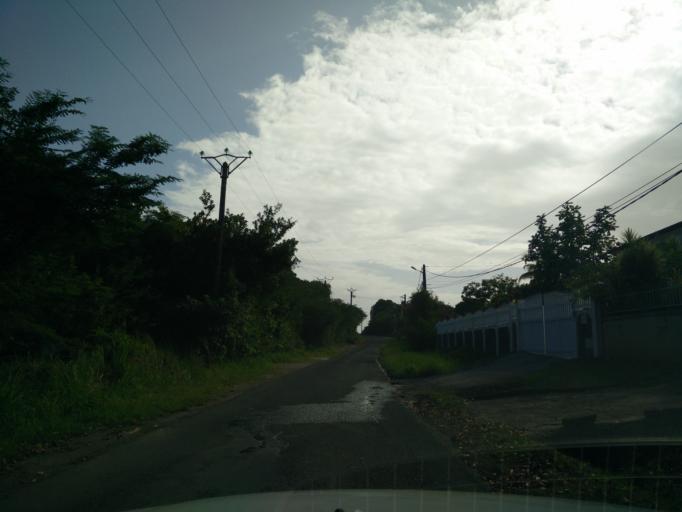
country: GP
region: Guadeloupe
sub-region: Guadeloupe
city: Sainte-Anne
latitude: 16.2350
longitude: -61.3751
